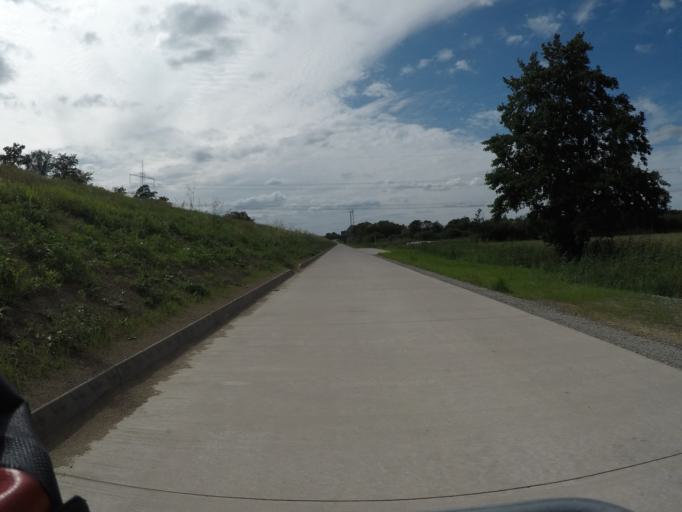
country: DE
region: Lower Saxony
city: Handorf
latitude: 53.3571
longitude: 10.3479
